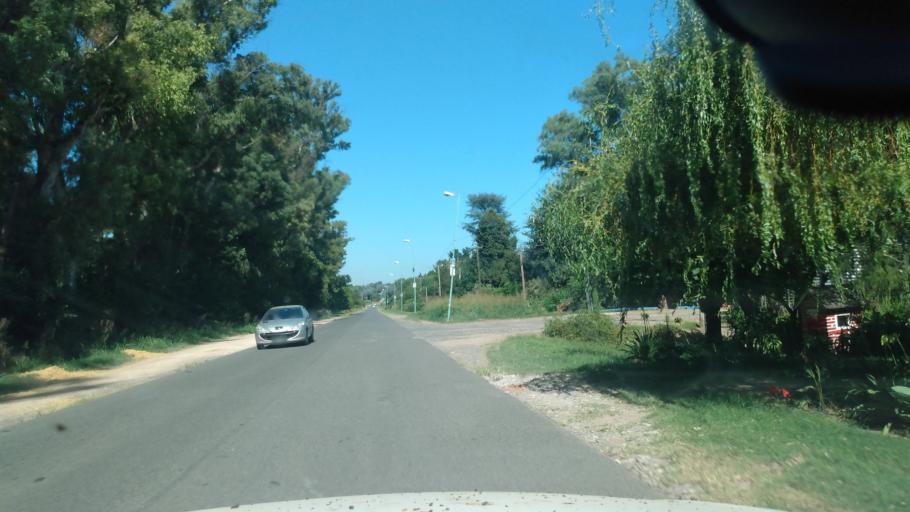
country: AR
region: Buenos Aires
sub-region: Partido de Lujan
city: Lujan
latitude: -34.5068
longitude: -59.0807
